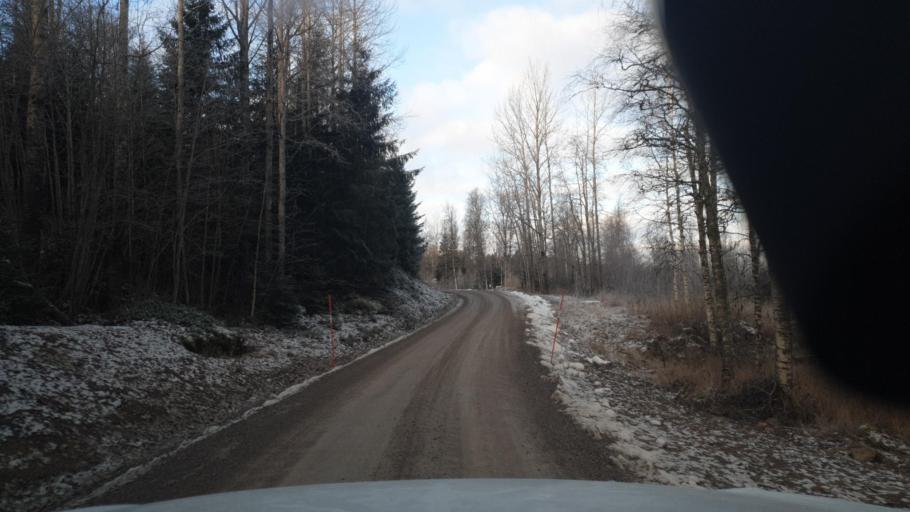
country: SE
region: Vaermland
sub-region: Eda Kommun
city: Charlottenberg
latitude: 60.0913
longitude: 12.4998
